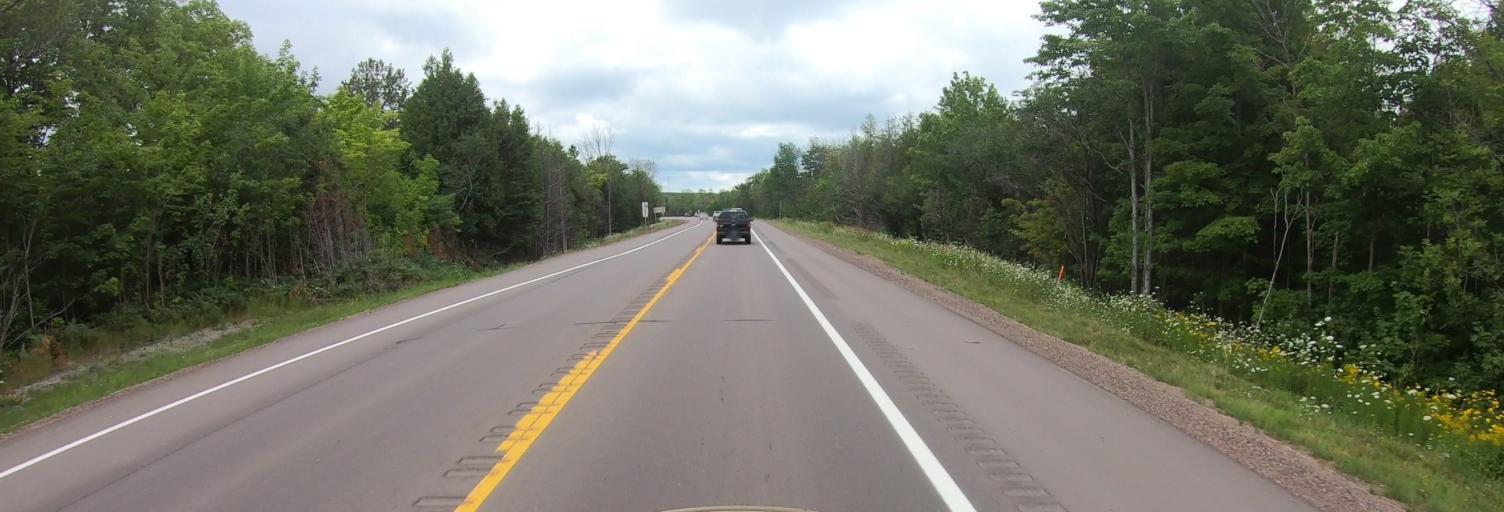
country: US
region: Michigan
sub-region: Houghton County
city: Houghton
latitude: 47.1551
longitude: -88.5575
